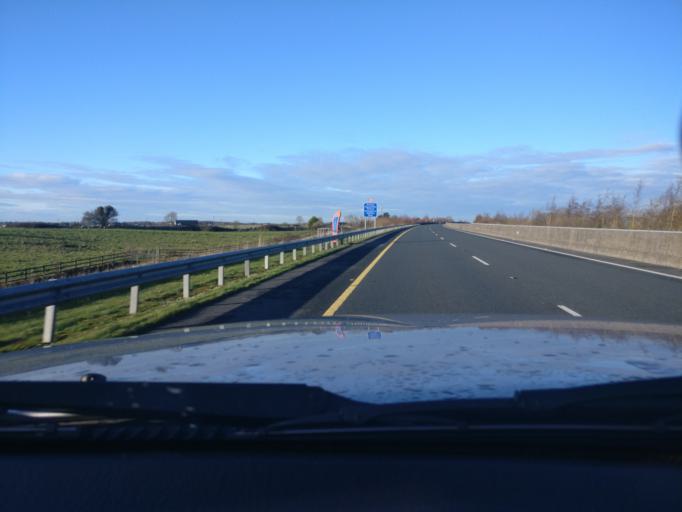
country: IE
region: Connaught
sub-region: County Galway
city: Athenry
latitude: 53.2701
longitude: -8.6668
